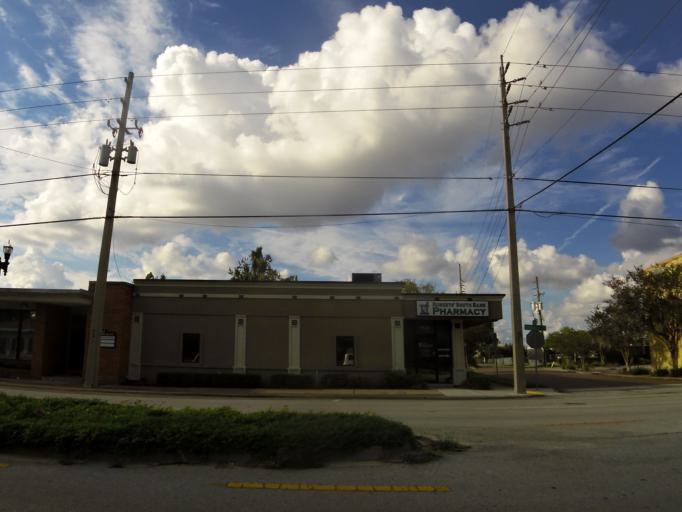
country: US
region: Florida
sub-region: Duval County
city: Jacksonville
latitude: 30.3059
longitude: -81.6512
